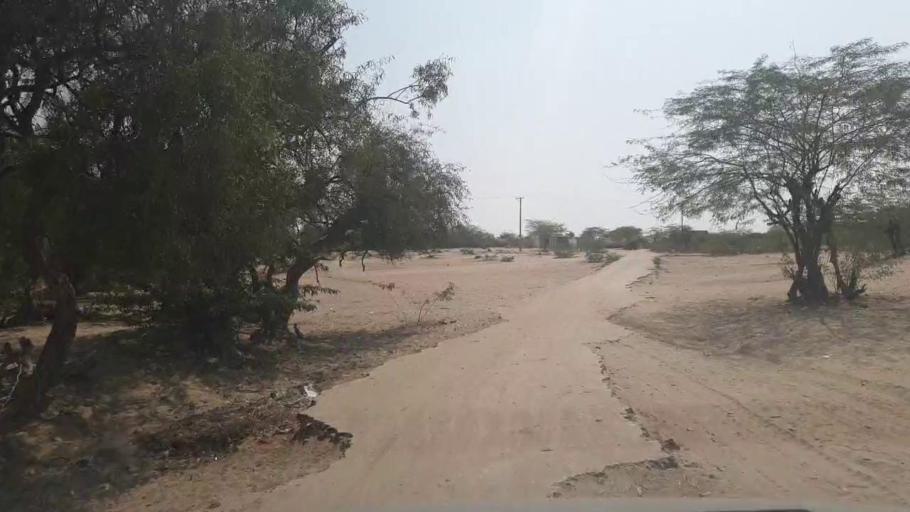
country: PK
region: Sindh
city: Chor
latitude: 25.4744
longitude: 69.7822
